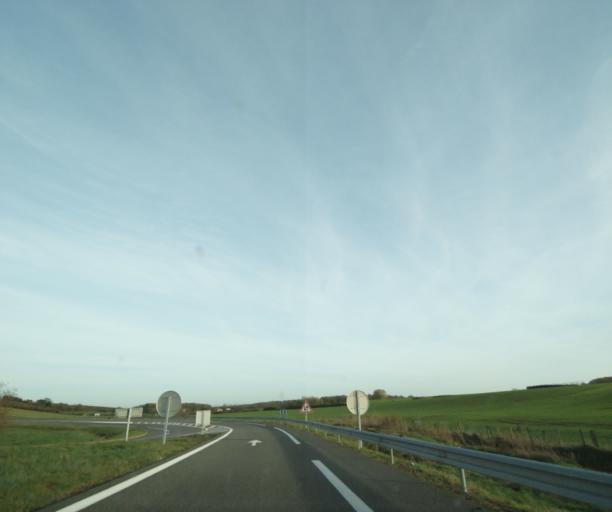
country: FR
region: Lorraine
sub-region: Departement de la Meuse
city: Etain
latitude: 49.1253
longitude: 5.6161
